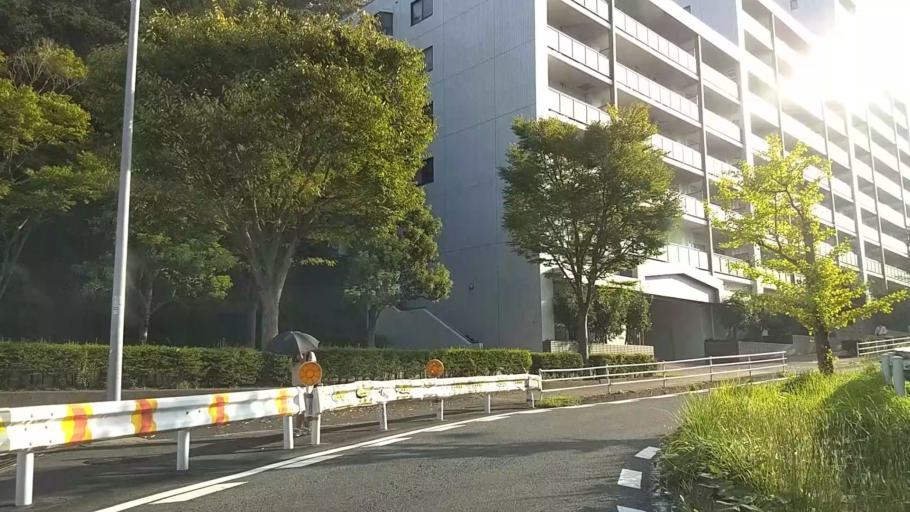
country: JP
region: Kanagawa
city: Yokohama
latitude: 35.4355
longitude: 139.5599
